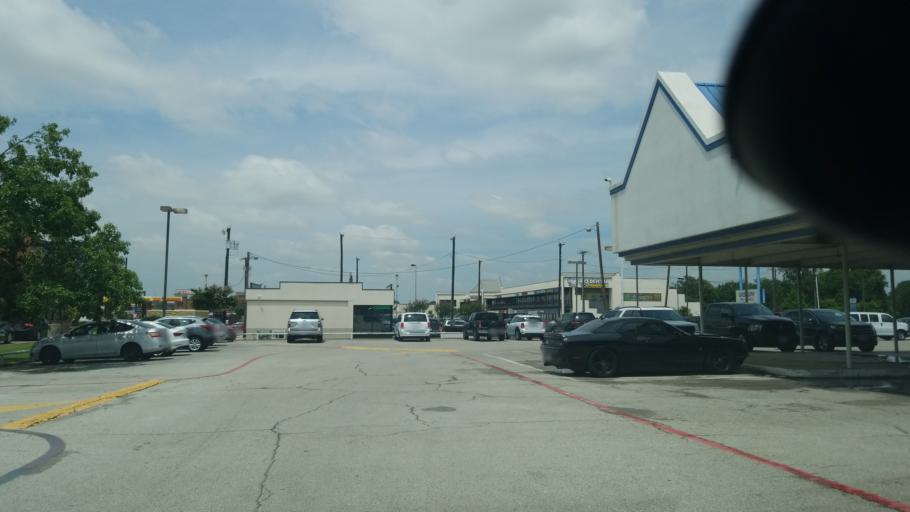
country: US
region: Texas
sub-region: Dallas County
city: Irving
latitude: 32.8380
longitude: -96.9581
